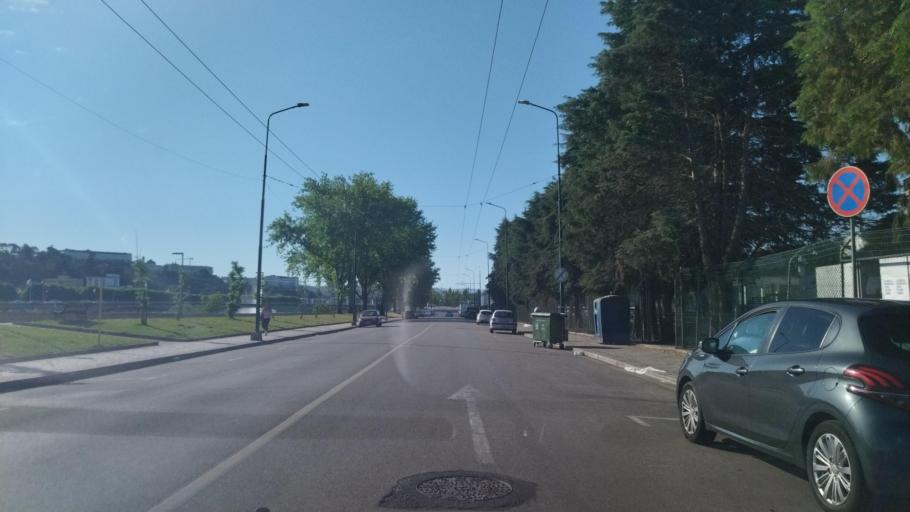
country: PT
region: Coimbra
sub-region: Coimbra
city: Coimbra
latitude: 40.2072
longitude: -8.4340
